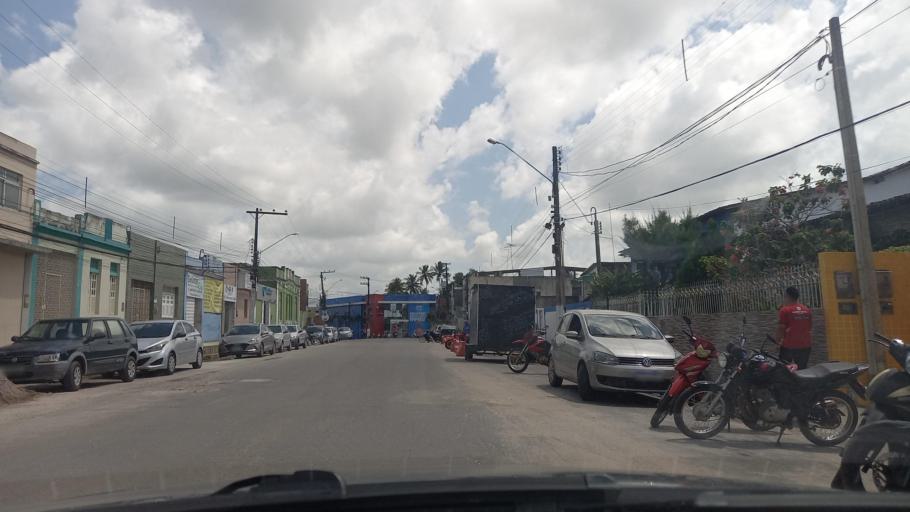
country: BR
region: Pernambuco
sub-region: Goiana
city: Goiana
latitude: -7.5584
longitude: -35.0036
